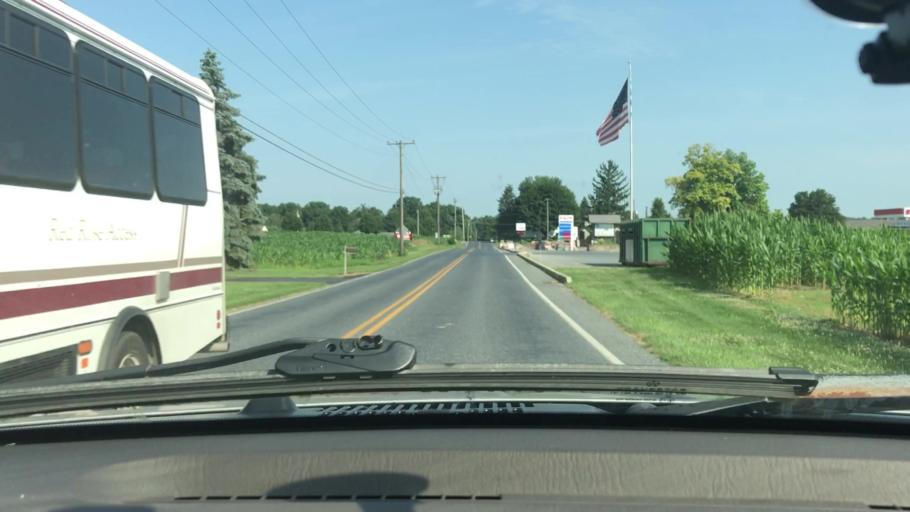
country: US
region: Pennsylvania
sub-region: Lancaster County
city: Rheems
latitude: 40.1613
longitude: -76.5725
